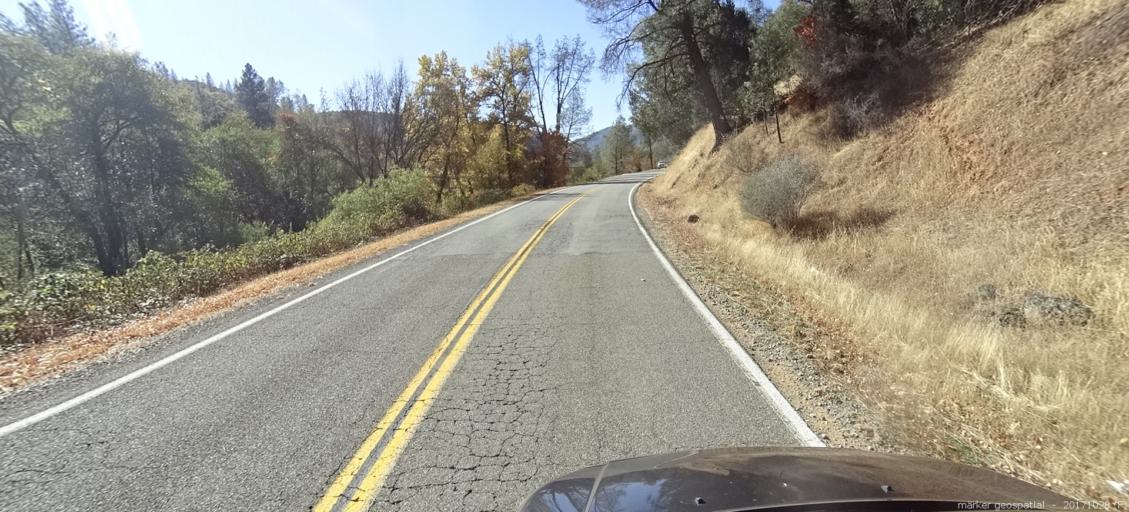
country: US
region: California
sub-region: Shasta County
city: Shasta
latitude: 40.7277
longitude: -122.6238
